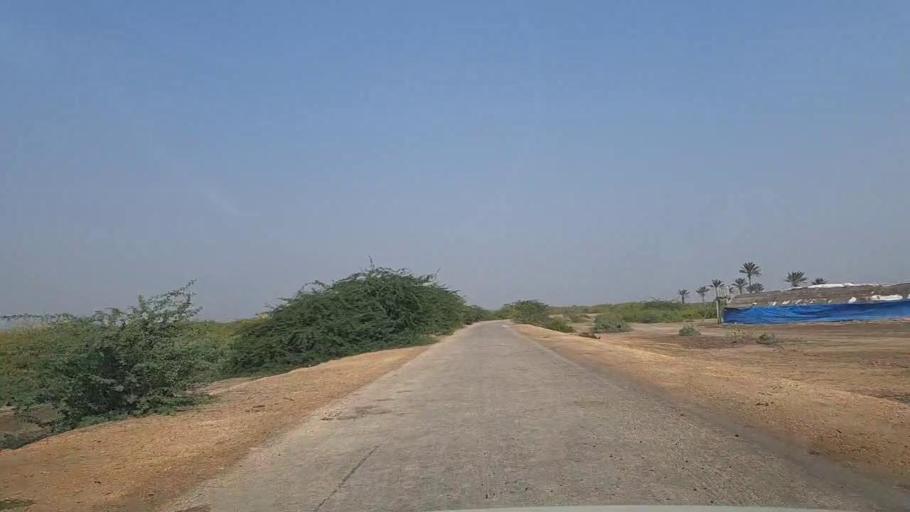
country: PK
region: Sindh
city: Keti Bandar
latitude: 24.2481
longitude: 67.7120
